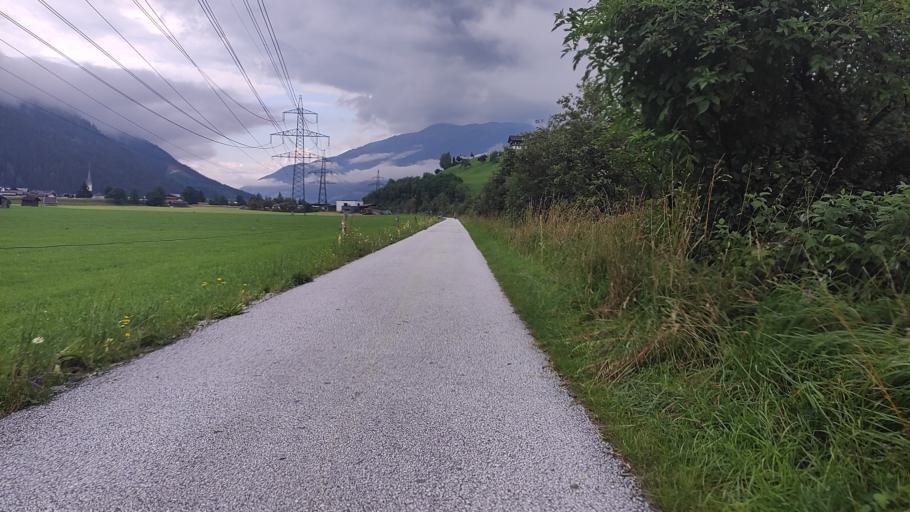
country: AT
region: Salzburg
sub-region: Politischer Bezirk Zell am See
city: Hollersbach im Pinzgau
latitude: 47.2786
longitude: 12.4305
